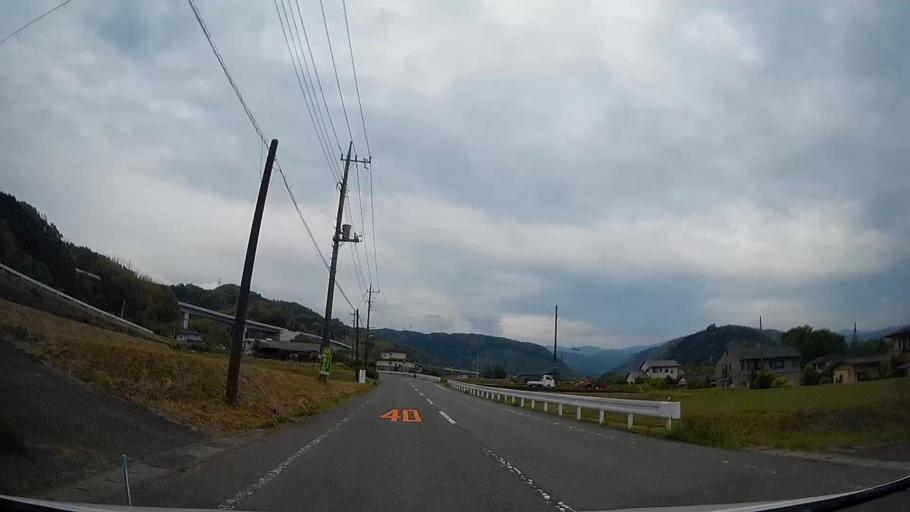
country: JP
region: Shizuoka
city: Ito
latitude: 34.9282
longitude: 138.9357
